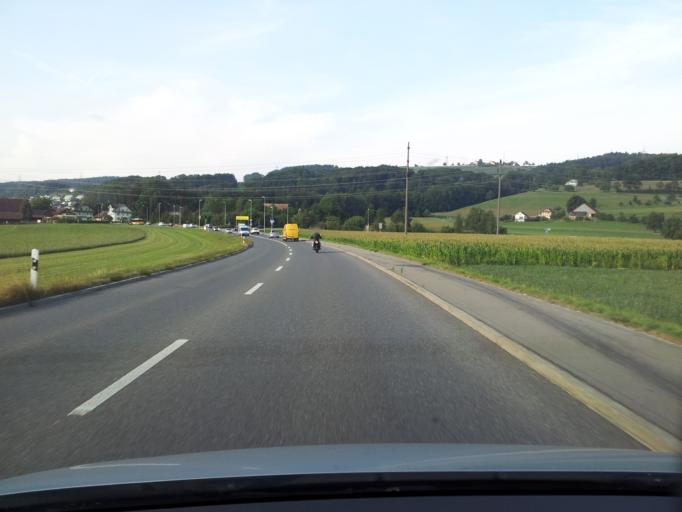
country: CH
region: Lucerne
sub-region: Sursee District
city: Geuensee
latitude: 47.1864
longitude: 8.1138
